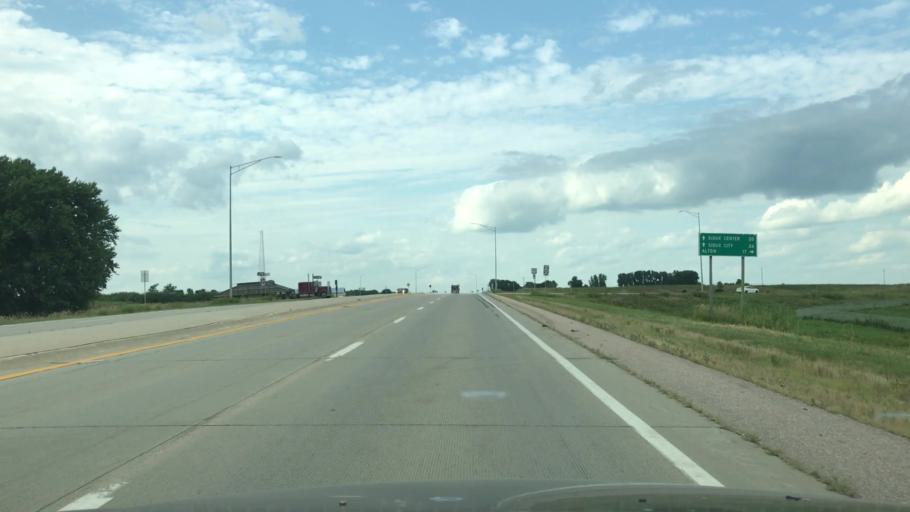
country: US
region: Iowa
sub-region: Plymouth County
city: Le Mars
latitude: 42.8154
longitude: -96.1746
